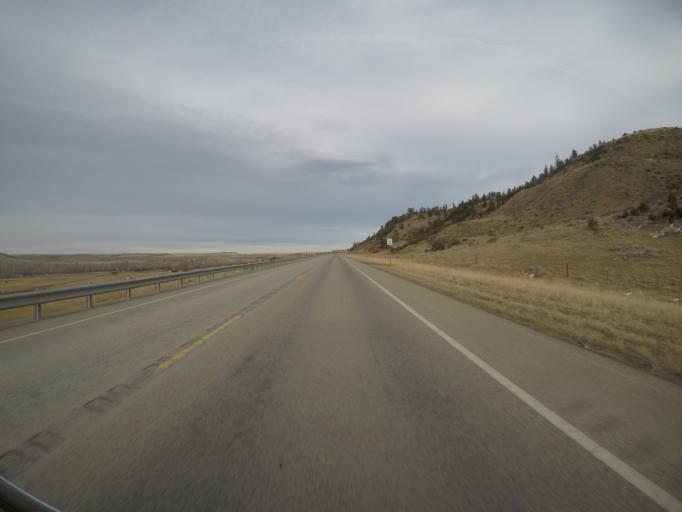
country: US
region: Montana
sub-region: Stillwater County
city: Absarokee
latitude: 45.5257
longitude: -109.4329
